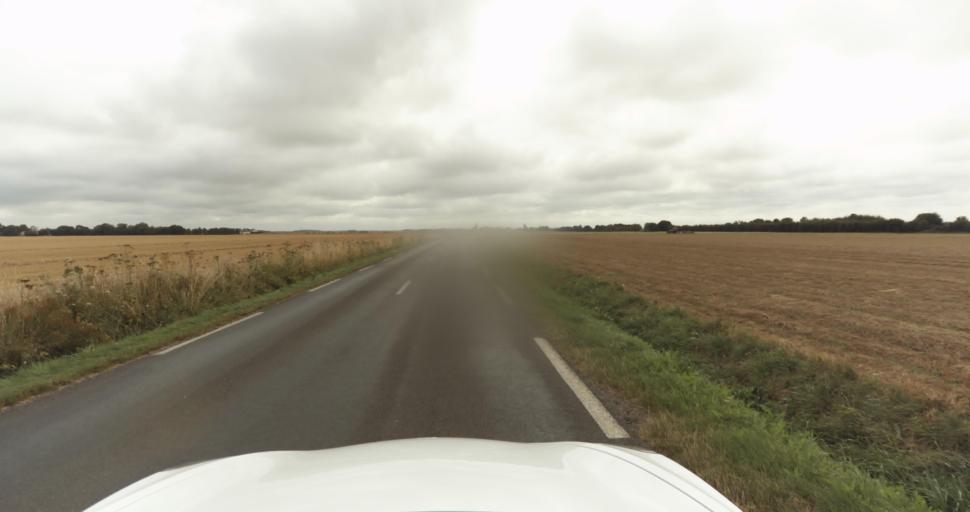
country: FR
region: Haute-Normandie
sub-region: Departement de l'Eure
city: Claville
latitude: 49.0797
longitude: 1.0569
